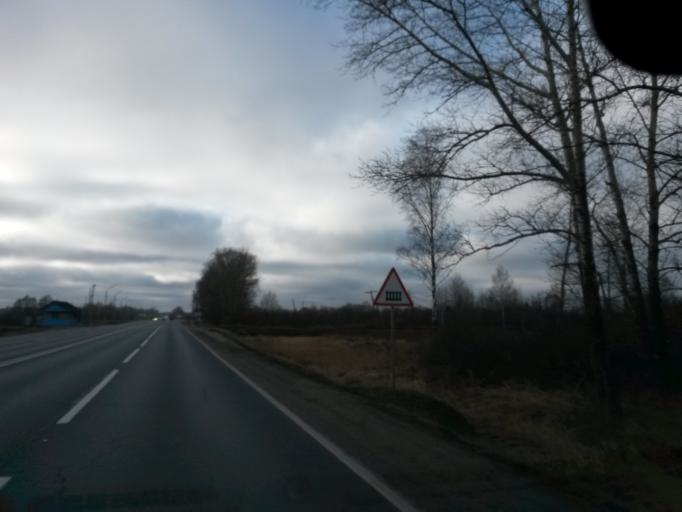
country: RU
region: Jaroslavl
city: Semibratovo
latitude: 57.3114
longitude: 39.5513
